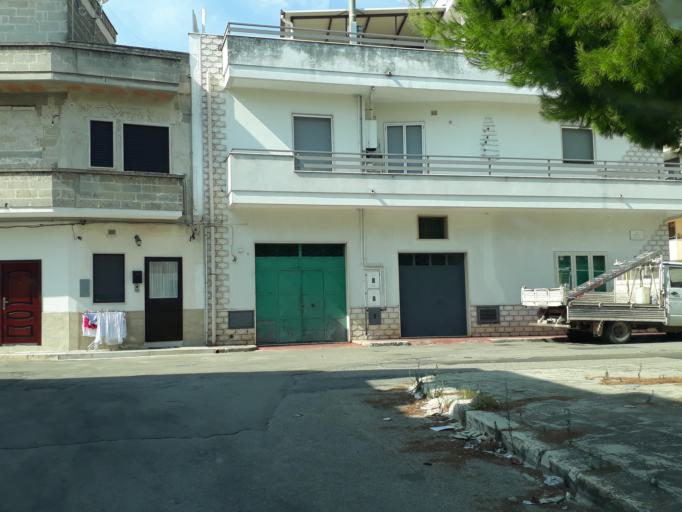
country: IT
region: Apulia
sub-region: Provincia di Brindisi
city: Carovigno
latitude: 40.7010
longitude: 17.6668
